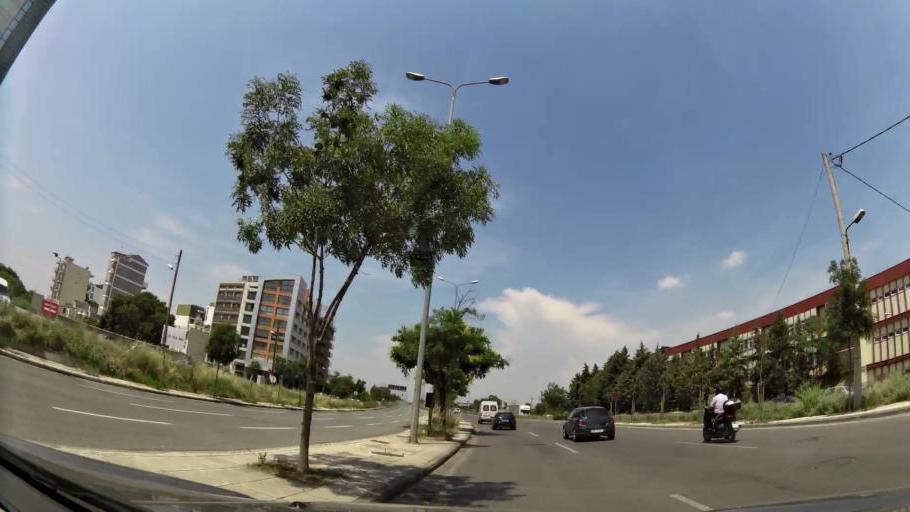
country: GR
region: Central Macedonia
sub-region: Nomos Thessalonikis
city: Ampelokipoi
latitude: 40.6461
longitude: 22.9177
